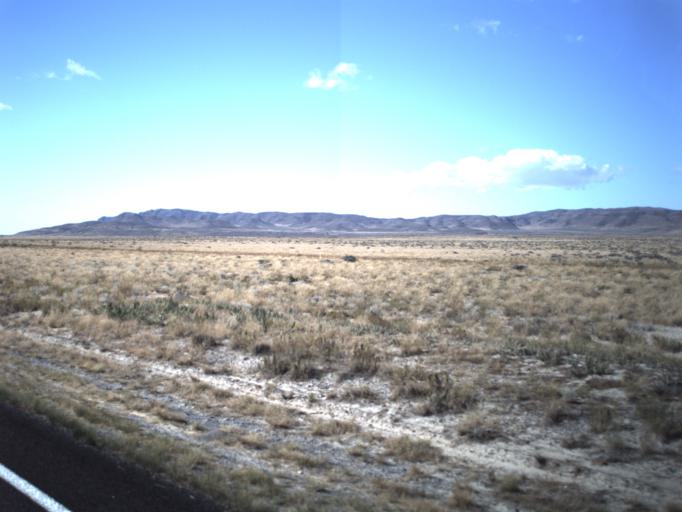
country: US
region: Utah
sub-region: Millard County
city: Delta
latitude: 38.9220
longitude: -112.8116
